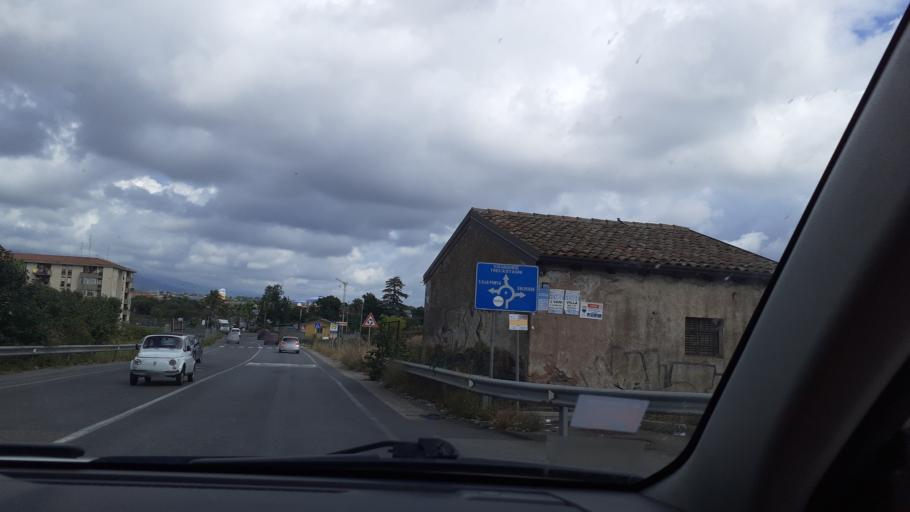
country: IT
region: Sicily
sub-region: Catania
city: San Giovanni la Punta
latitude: 37.5763
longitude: 15.1035
